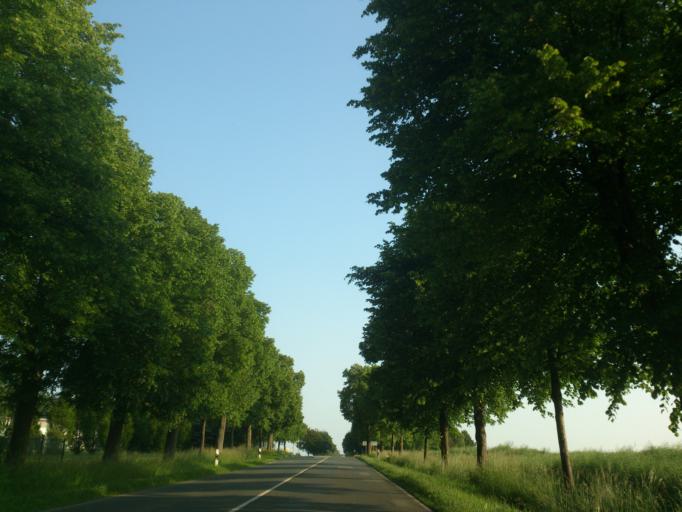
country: DE
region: North Rhine-Westphalia
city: Lichtenau
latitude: 51.6211
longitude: 8.8880
